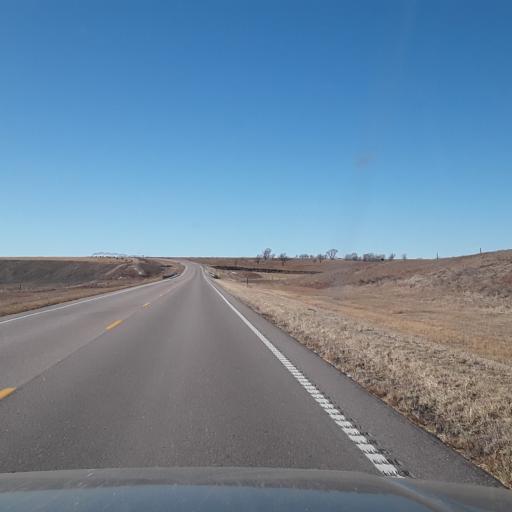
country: US
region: Nebraska
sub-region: Frontier County
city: Stockville
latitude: 40.7057
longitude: -100.2371
